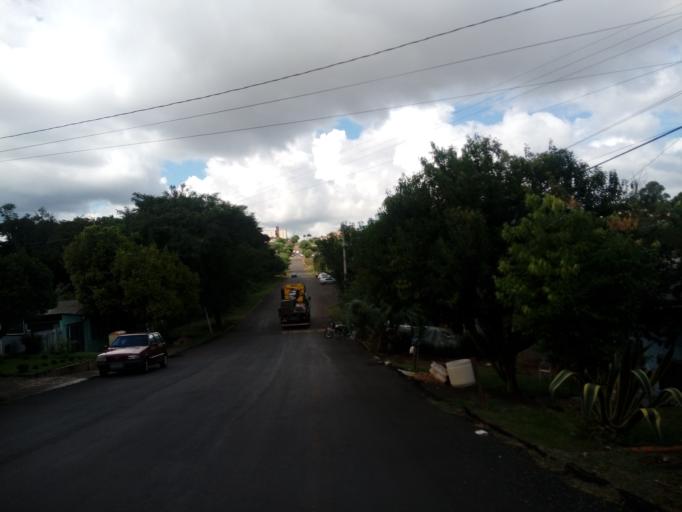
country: BR
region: Santa Catarina
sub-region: Chapeco
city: Chapeco
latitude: -27.0859
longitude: -52.6070
